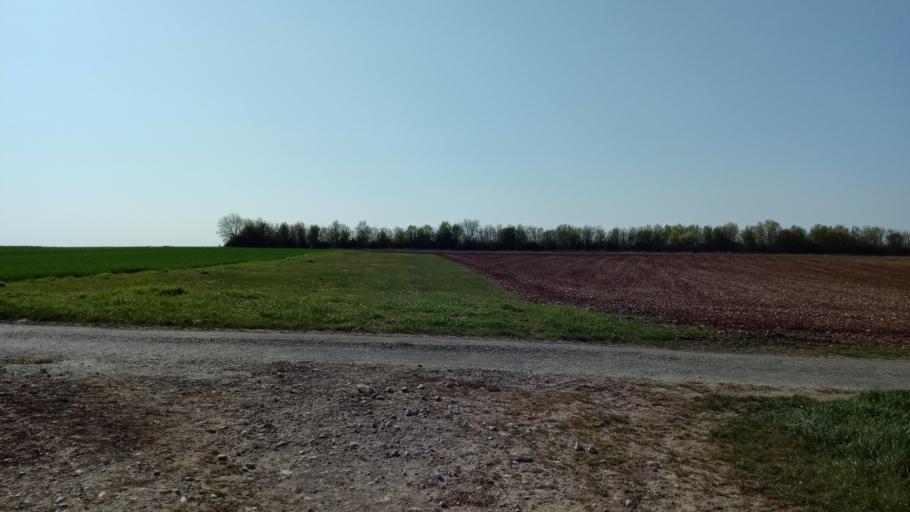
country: FR
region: Poitou-Charentes
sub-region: Departement de la Charente-Maritime
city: Verines
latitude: 46.1578
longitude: -0.9343
